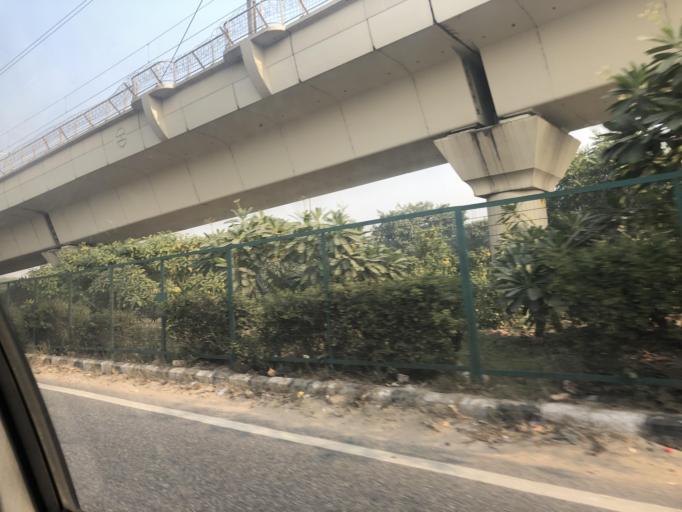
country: IN
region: NCT
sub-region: Central Delhi
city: Karol Bagh
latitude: 28.6108
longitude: 77.1385
